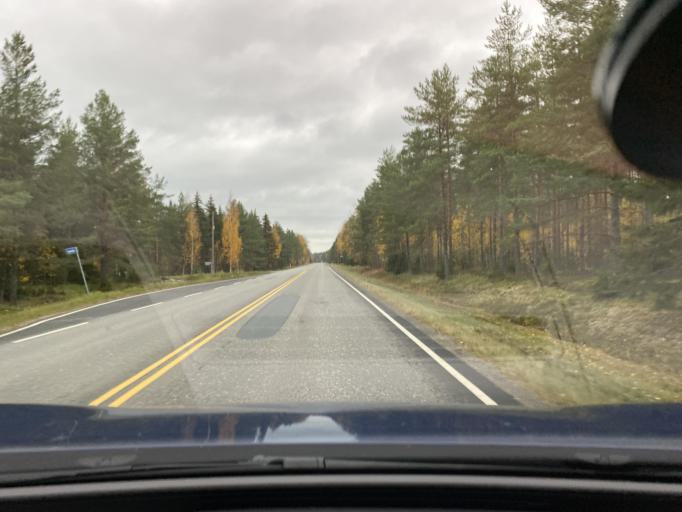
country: FI
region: Varsinais-Suomi
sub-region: Loimaa
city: Ylaene
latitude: 60.9091
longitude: 22.4113
